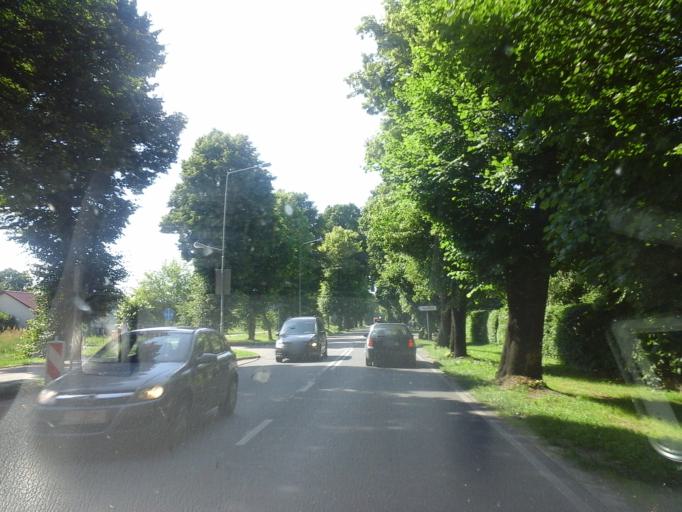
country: PL
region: West Pomeranian Voivodeship
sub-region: Powiat bialogardzki
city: Bialogard
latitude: 54.0143
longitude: 15.9570
